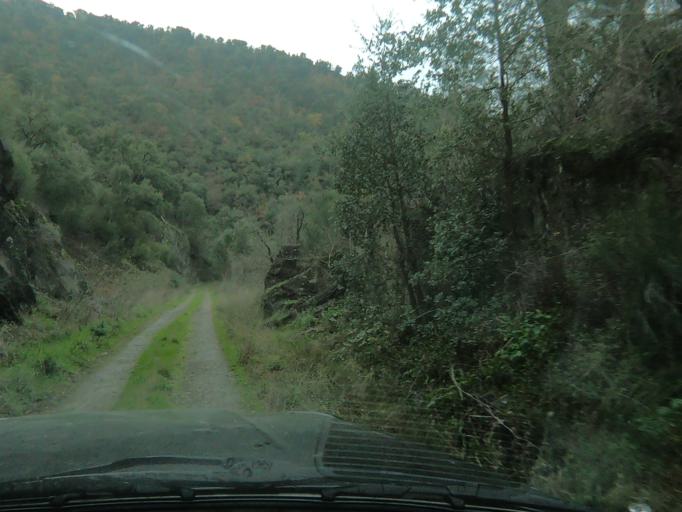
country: PT
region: Vila Real
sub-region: Santa Marta de Penaguiao
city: Santa Marta de Penaguiao
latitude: 41.2145
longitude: -7.7569
